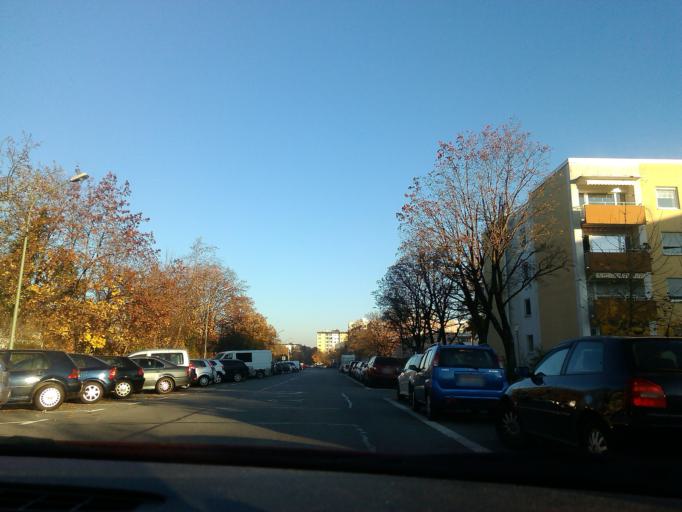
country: DE
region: Bavaria
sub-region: Upper Bavaria
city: Pasing
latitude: 48.1257
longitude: 11.4729
